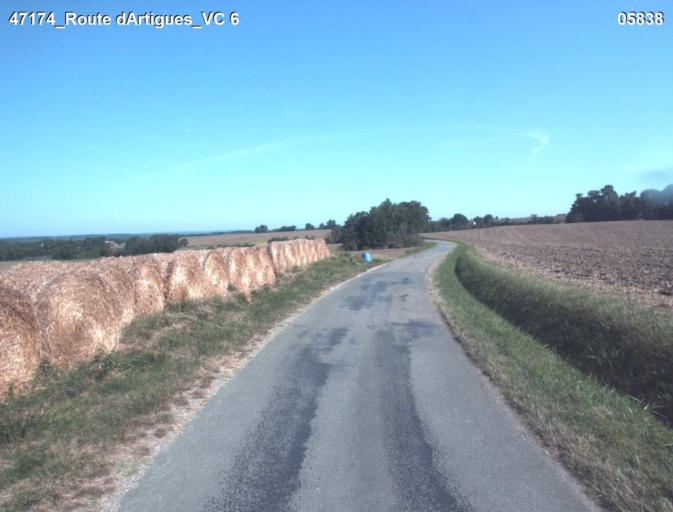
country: FR
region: Aquitaine
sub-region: Departement du Lot-et-Garonne
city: Mezin
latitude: 44.0509
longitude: 0.3311
